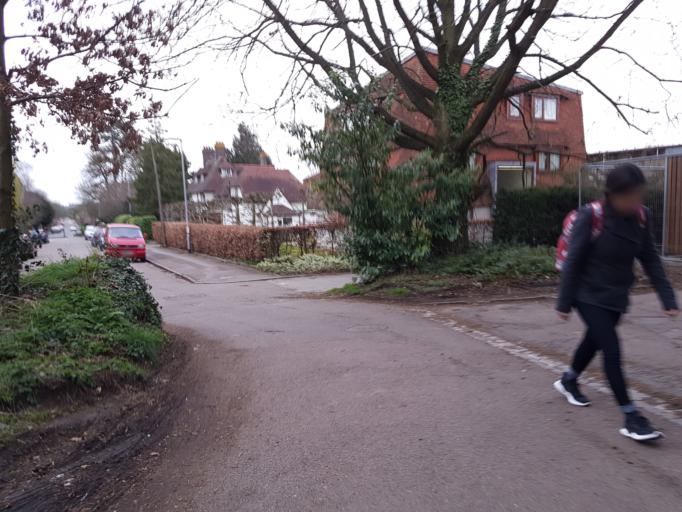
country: GB
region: England
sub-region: Cambridgeshire
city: Girton
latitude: 52.2160
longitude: 0.0986
